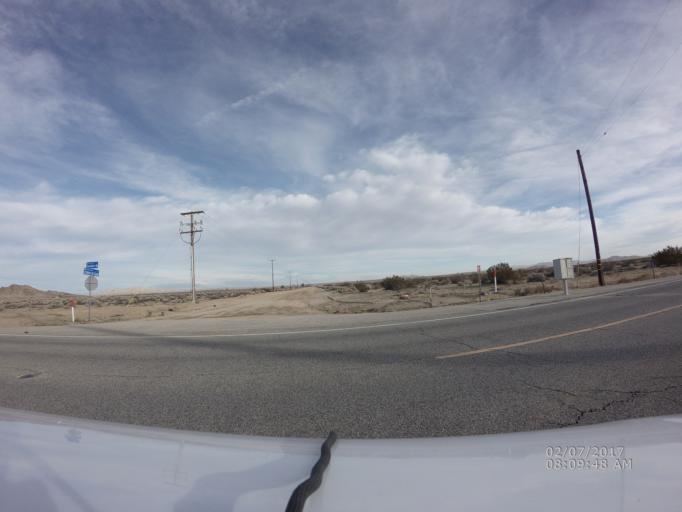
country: US
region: California
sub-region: Los Angeles County
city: Lake Los Angeles
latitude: 34.5771
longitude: -117.7206
